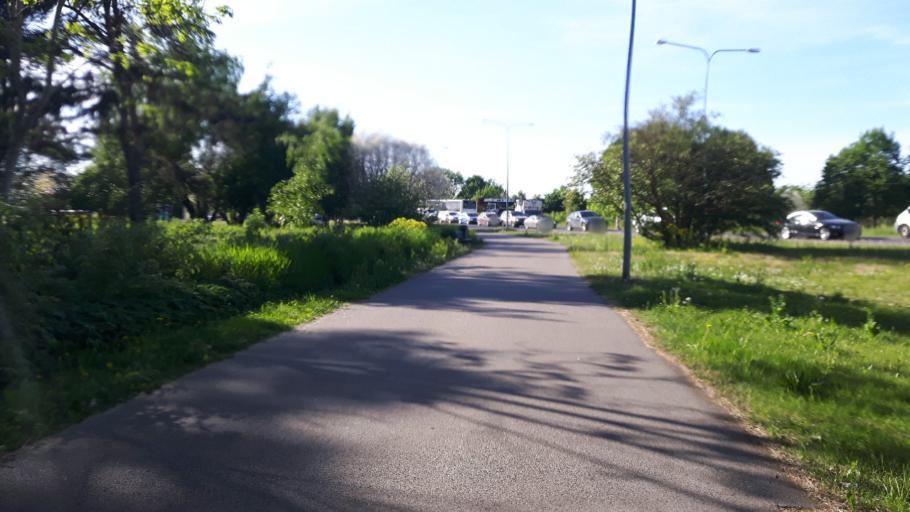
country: EE
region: Harju
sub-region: Tallinna linn
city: Kose
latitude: 59.4514
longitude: 24.8552
